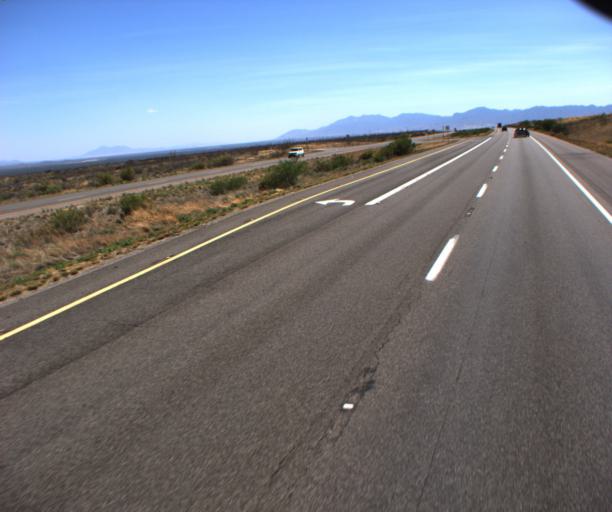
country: US
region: Arizona
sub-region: Cochise County
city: Whetstone
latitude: 31.8073
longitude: -110.3495
